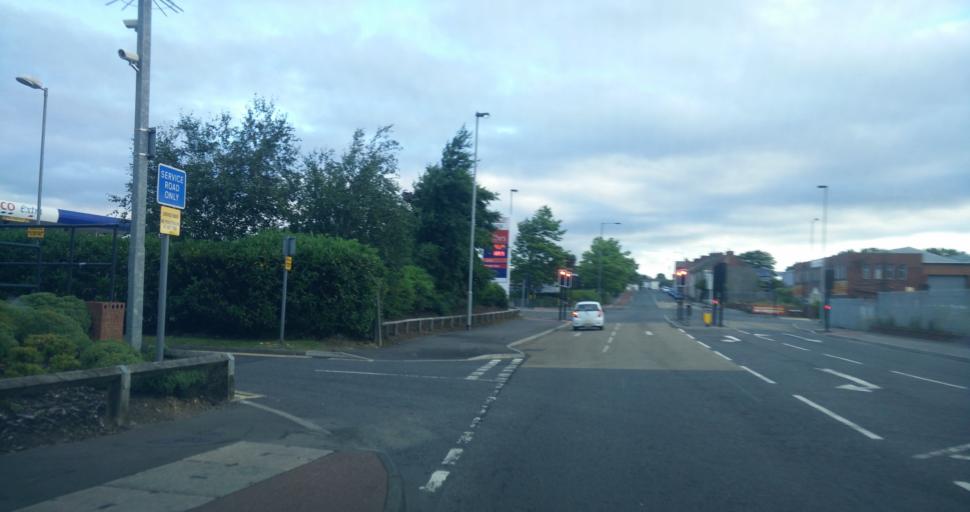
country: GB
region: England
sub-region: County Durham
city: Durham
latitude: 54.7771
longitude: -1.5398
